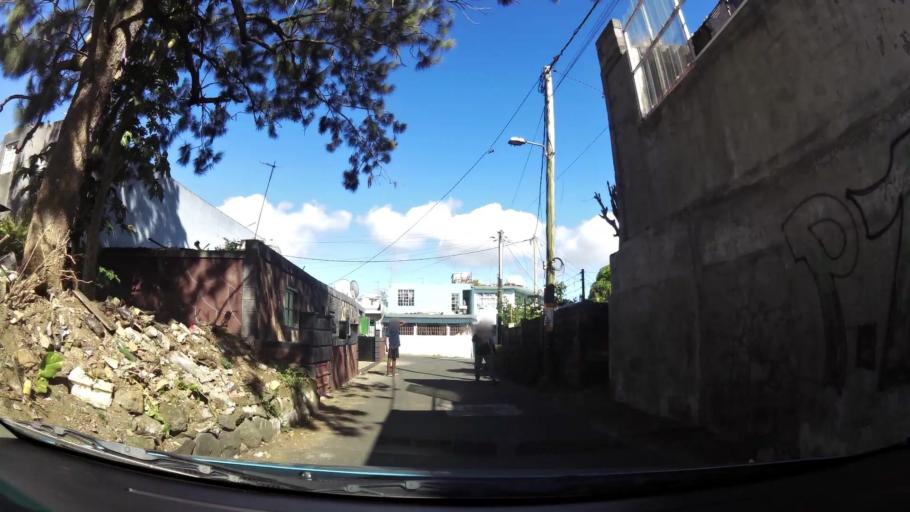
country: MU
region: Plaines Wilhems
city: Curepipe
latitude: -20.3043
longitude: 57.5043
